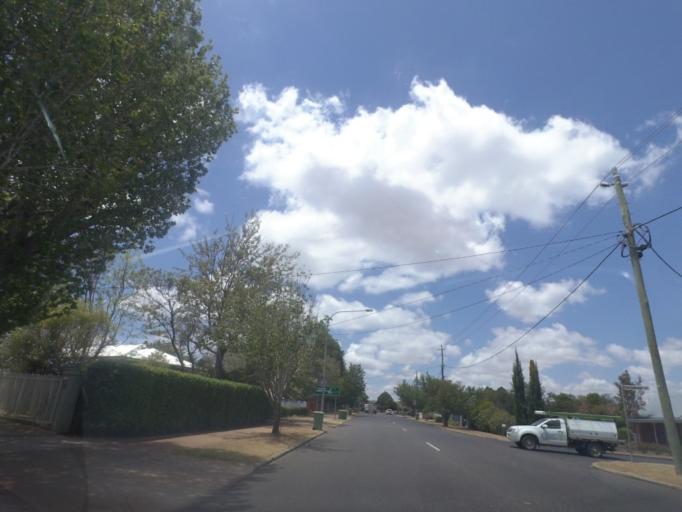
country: AU
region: Queensland
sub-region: Toowoomba
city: Rangeville
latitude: -27.5770
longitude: 151.9788
